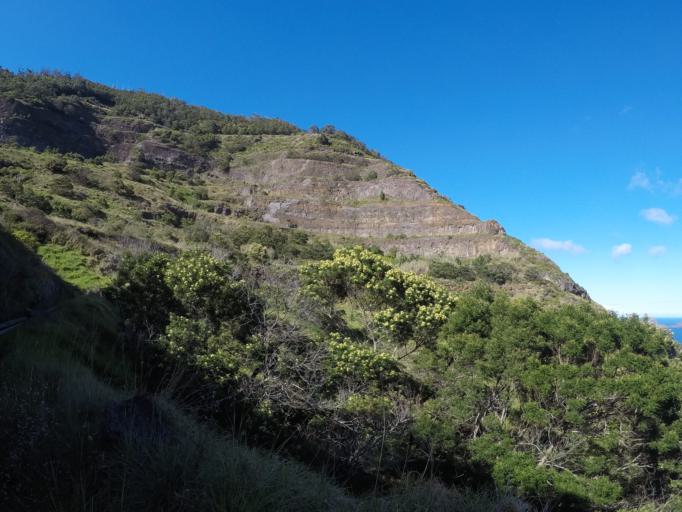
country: PT
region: Madeira
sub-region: Machico
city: Canical
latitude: 32.7385
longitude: -16.7550
